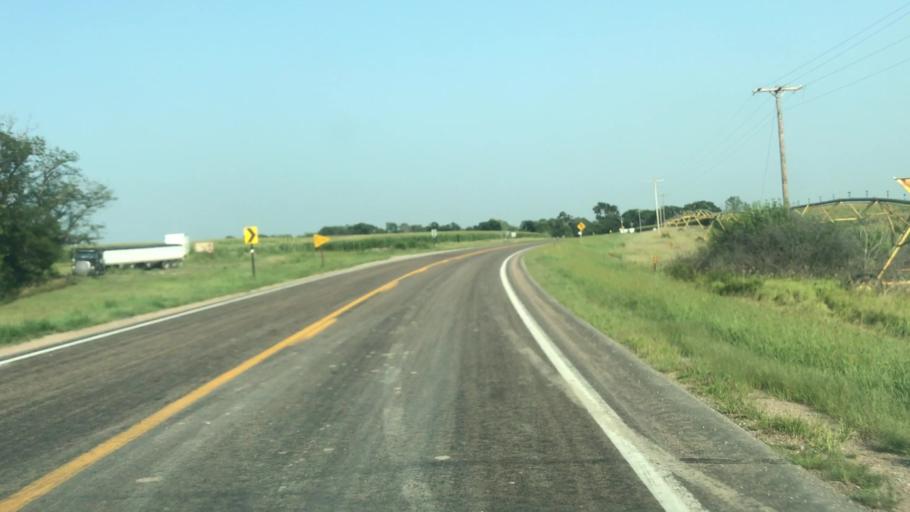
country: US
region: Nebraska
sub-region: Buffalo County
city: Ravenna
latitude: 41.0756
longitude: -98.7294
